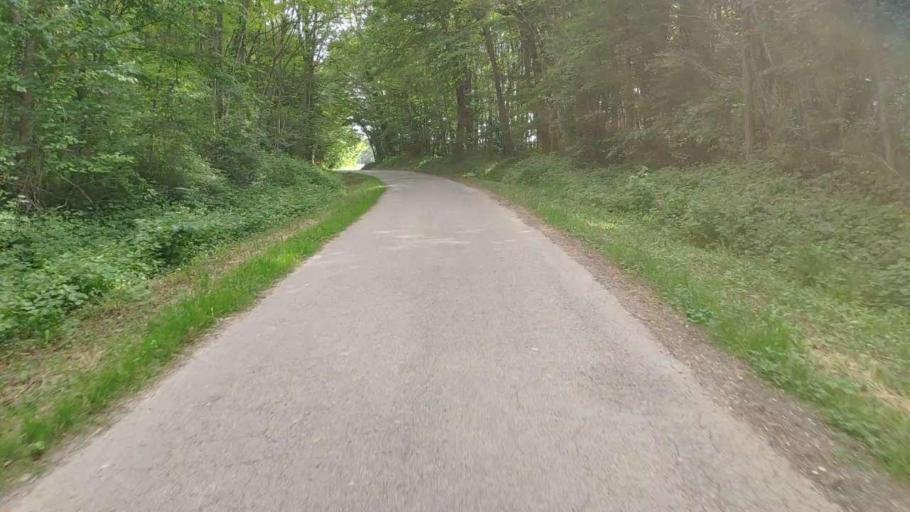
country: FR
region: Franche-Comte
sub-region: Departement du Jura
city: Petit-Noir
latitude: 46.8169
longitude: 5.3570
